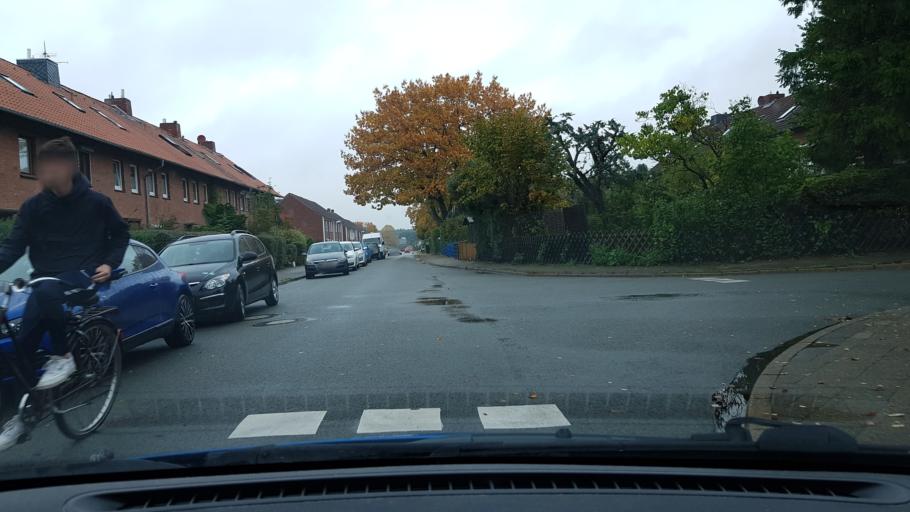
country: DE
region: Lower Saxony
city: Lueneburg
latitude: 53.2483
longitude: 10.4412
